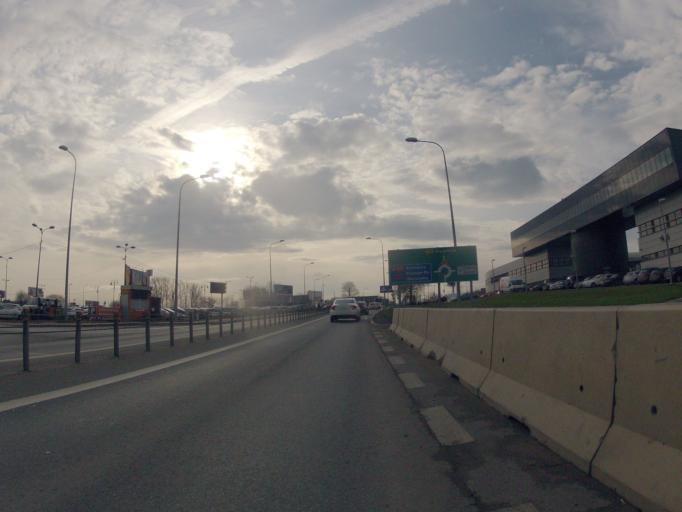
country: PL
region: Lesser Poland Voivodeship
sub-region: Powiat krakowski
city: Balice
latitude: 50.0738
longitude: 19.8067
